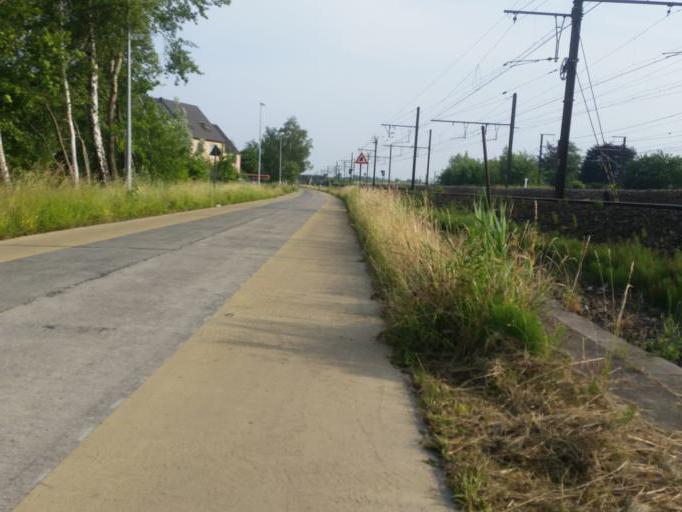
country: BE
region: Flanders
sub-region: Provincie Antwerpen
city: Duffel
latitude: 51.0681
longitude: 4.4961
